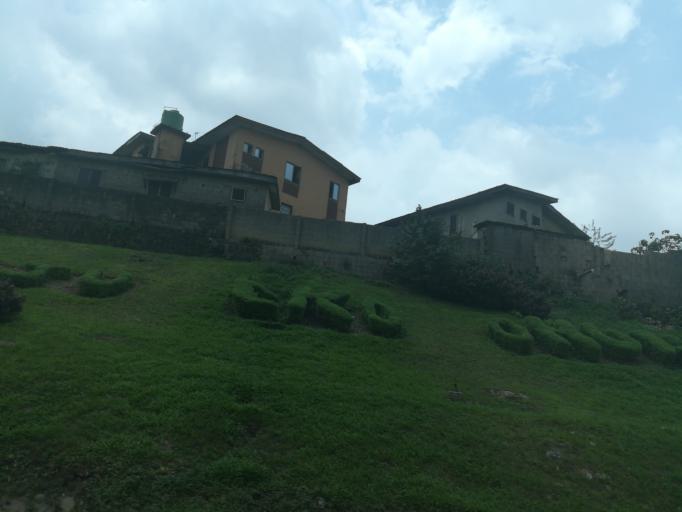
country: NG
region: Lagos
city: Ojota
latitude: 6.5732
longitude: 3.3973
